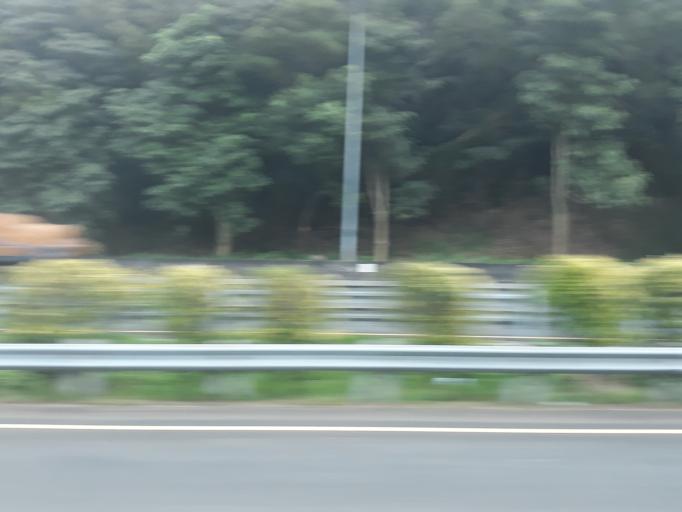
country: TW
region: Taiwan
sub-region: Miaoli
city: Miaoli
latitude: 24.4232
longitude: 120.7764
